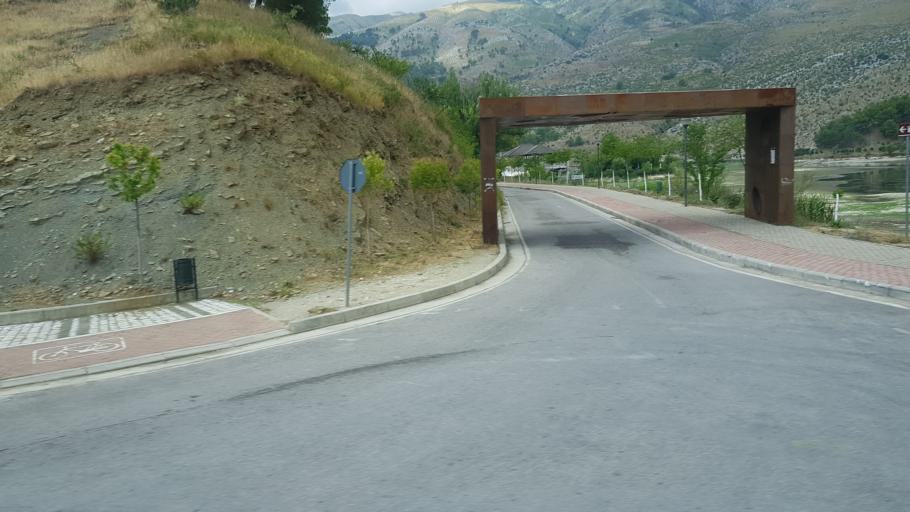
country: AL
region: Gjirokaster
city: Gjirokaster
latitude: 40.1015
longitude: 20.1274
